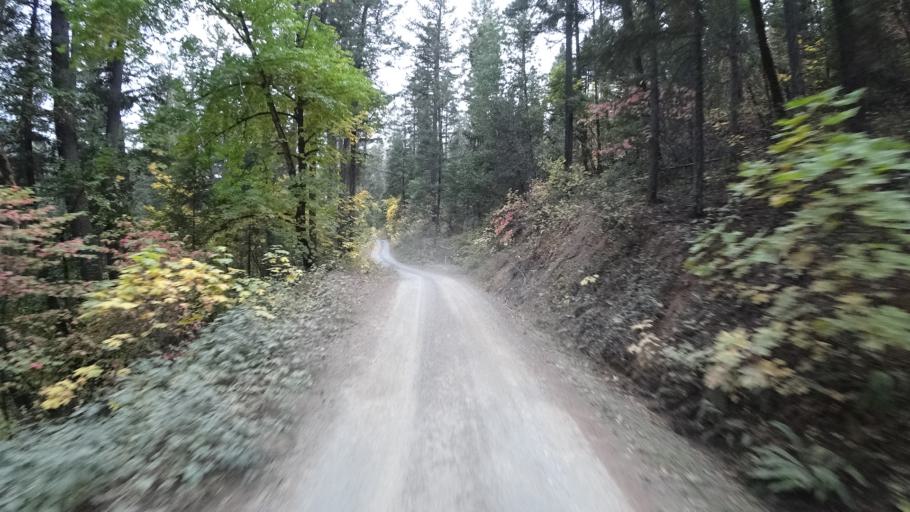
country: US
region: California
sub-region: Siskiyou County
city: Happy Camp
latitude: 41.7882
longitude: -123.3357
